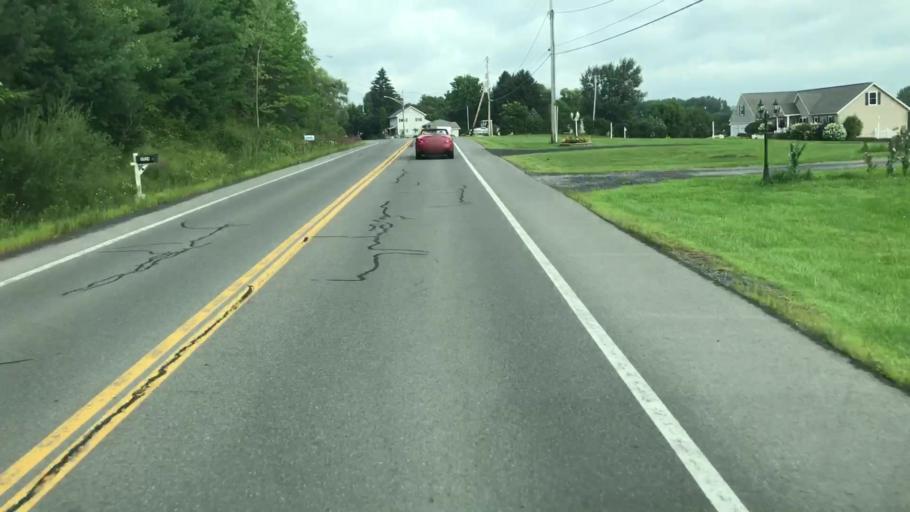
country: US
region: New York
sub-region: Onondaga County
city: Camillus
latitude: 43.0553
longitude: -76.3152
